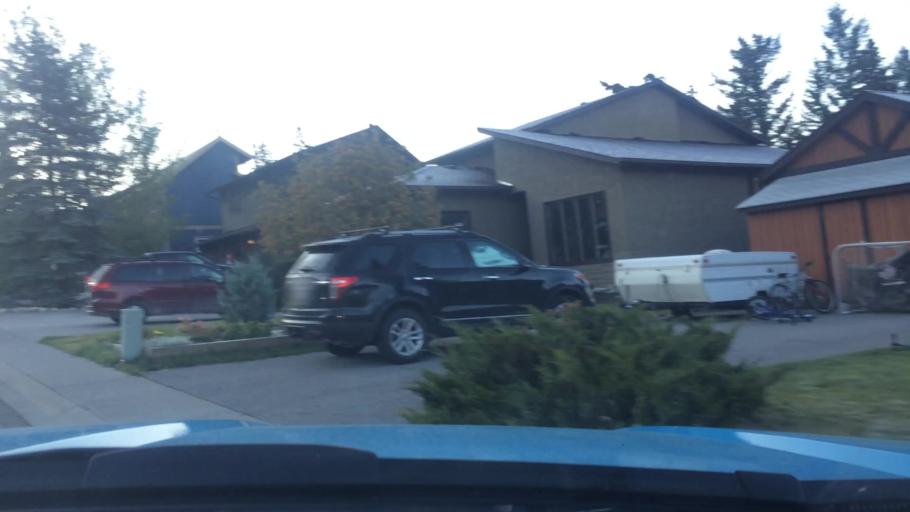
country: CA
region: Alberta
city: Canmore
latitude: 51.0862
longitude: -115.3332
